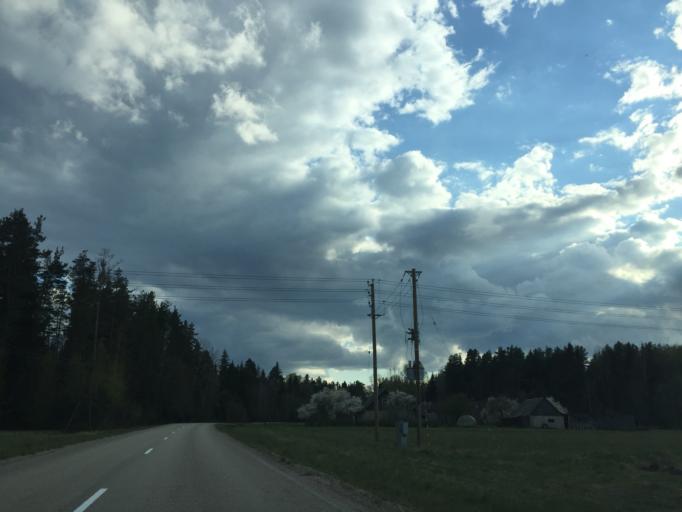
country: LV
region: Priekuli
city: Priekuli
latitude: 57.3768
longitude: 25.4156
